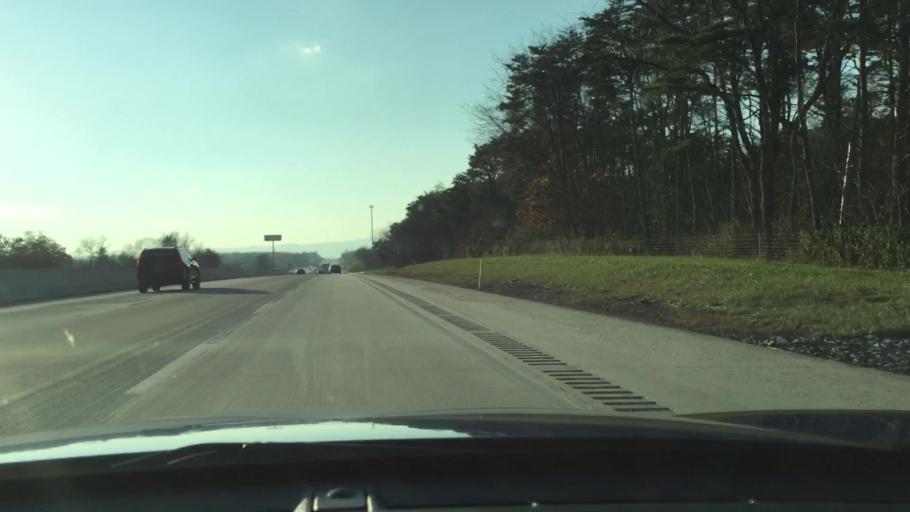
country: US
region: Pennsylvania
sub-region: Cumberland County
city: Newville
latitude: 40.1877
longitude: -77.4679
